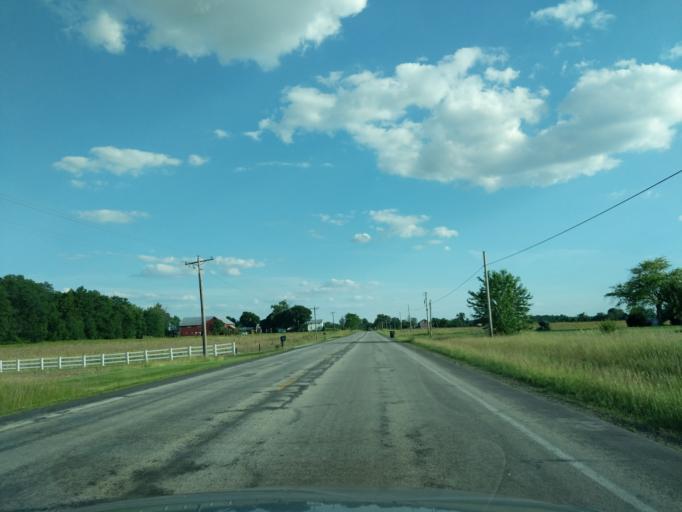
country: US
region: Indiana
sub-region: Whitley County
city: Columbia City
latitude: 41.0971
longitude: -85.4715
